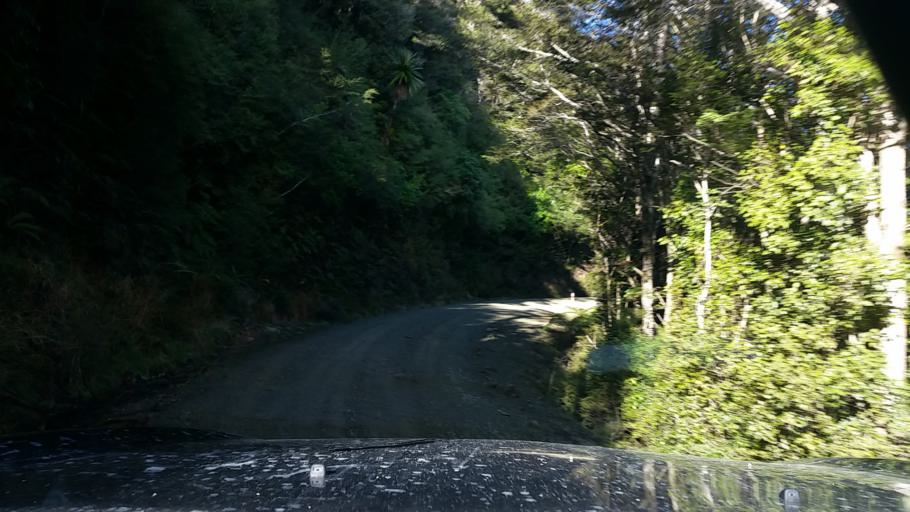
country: NZ
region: Marlborough
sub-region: Marlborough District
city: Picton
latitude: -41.0855
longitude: 174.1508
